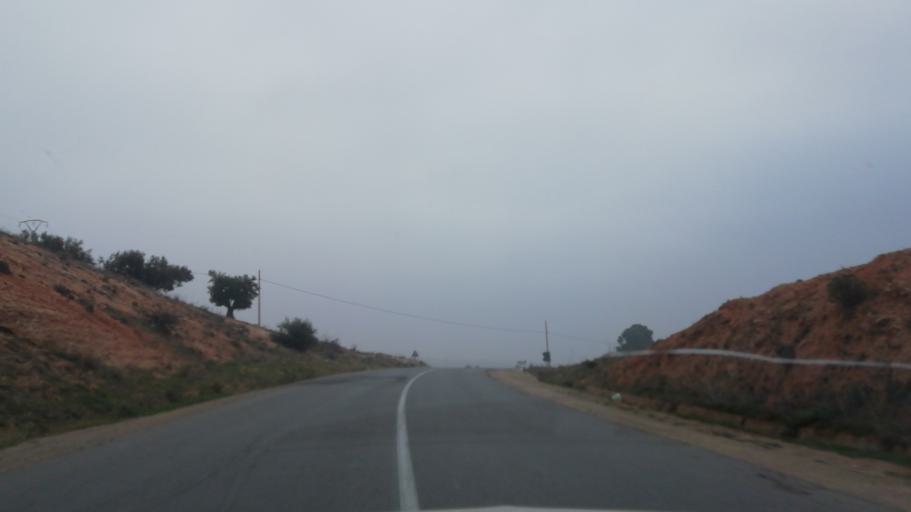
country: DZ
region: Mascara
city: Mascara
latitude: 35.4123
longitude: 0.1578
